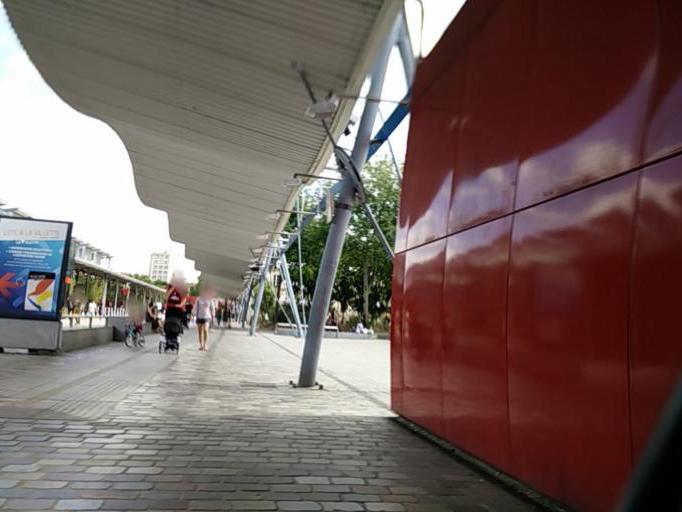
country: FR
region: Ile-de-France
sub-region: Departement de Seine-Saint-Denis
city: Le Pre-Saint-Gervais
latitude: 48.8908
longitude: 2.3902
